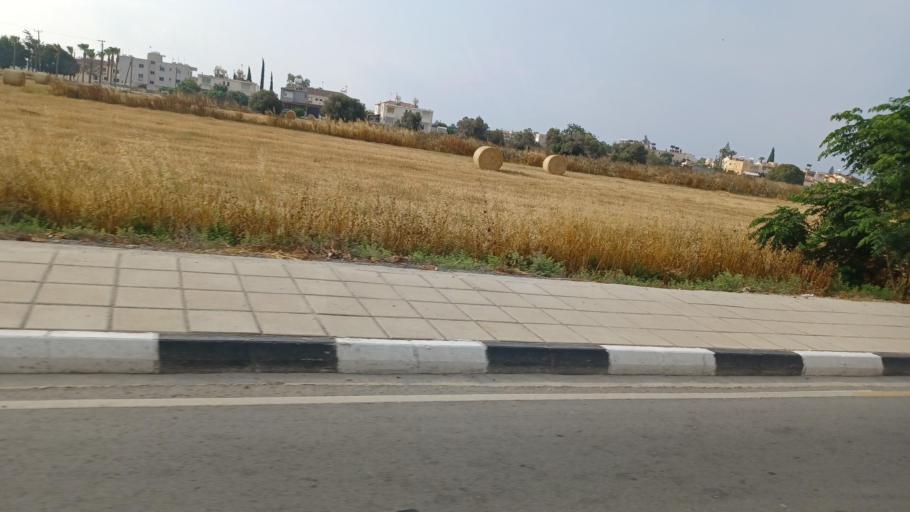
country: CY
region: Larnaka
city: Perivolia
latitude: 34.8320
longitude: 33.5831
